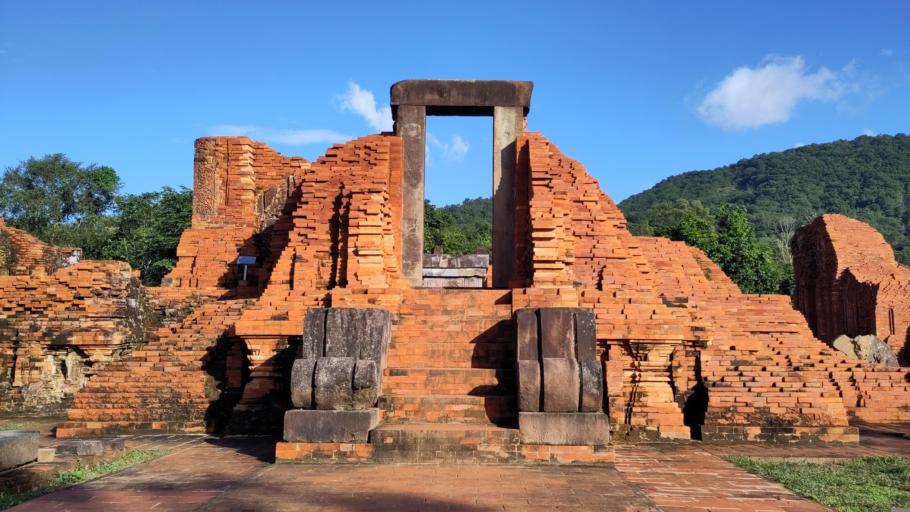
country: VN
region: Quang Nam
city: Dai Loc
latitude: 15.7626
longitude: 108.1249
